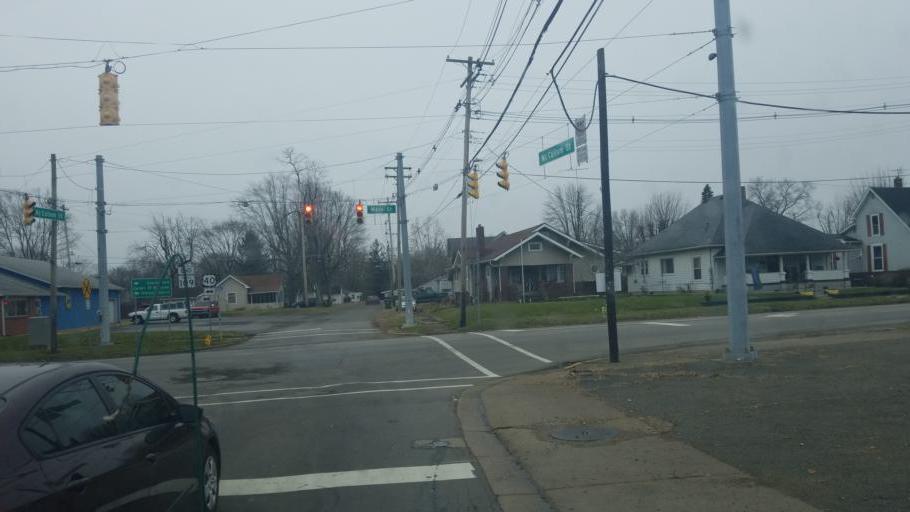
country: US
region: Indiana
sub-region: Henry County
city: Knightstown
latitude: 39.7951
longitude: -85.5322
